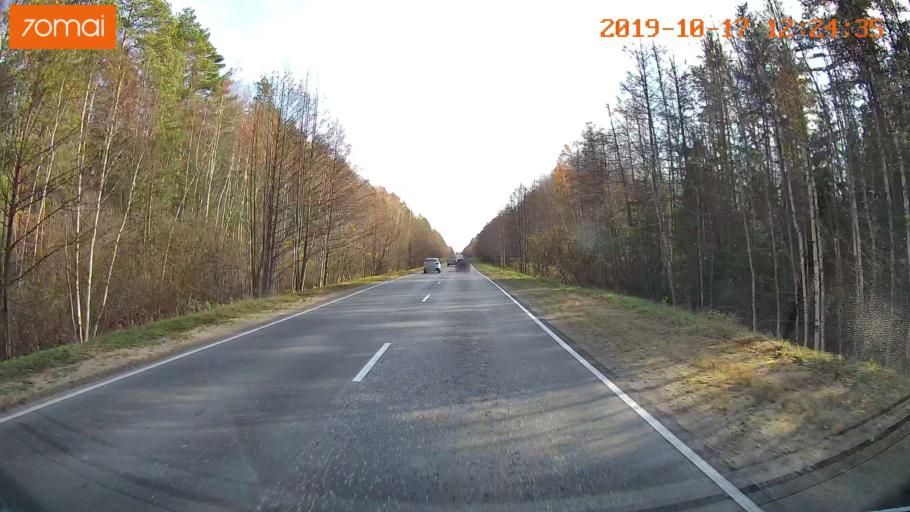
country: RU
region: Rjazan
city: Gus'-Zheleznyy
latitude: 55.0344
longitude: 41.2178
